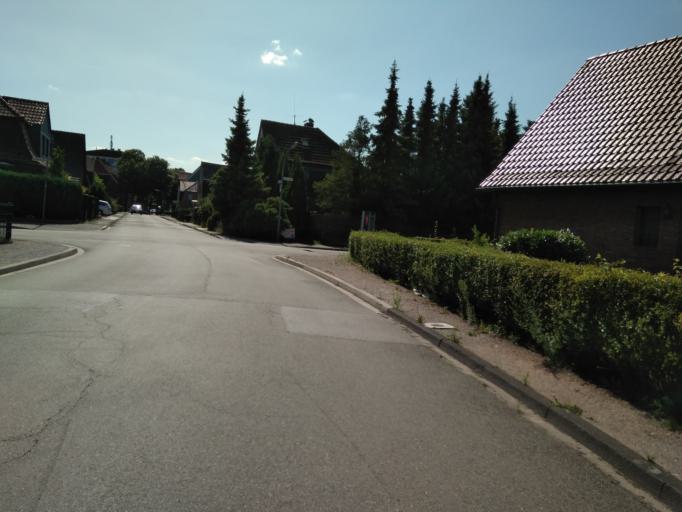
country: DE
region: North Rhine-Westphalia
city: Dorsten
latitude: 51.6859
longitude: 6.9560
